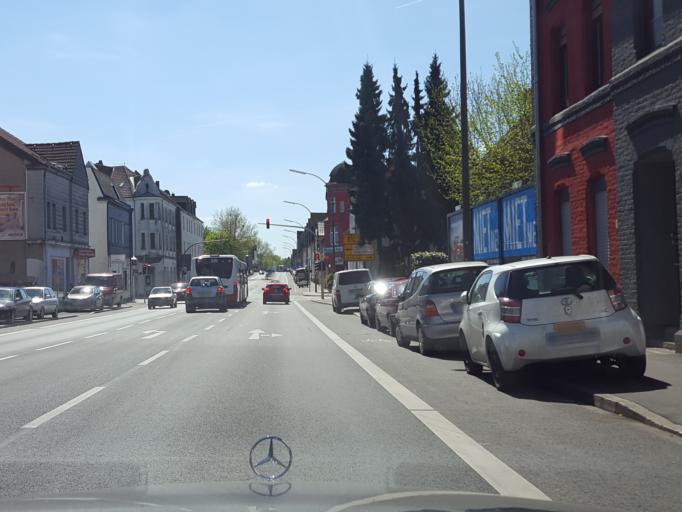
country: DE
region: North Rhine-Westphalia
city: Castrop-Rauxel
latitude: 51.5032
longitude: 7.3250
